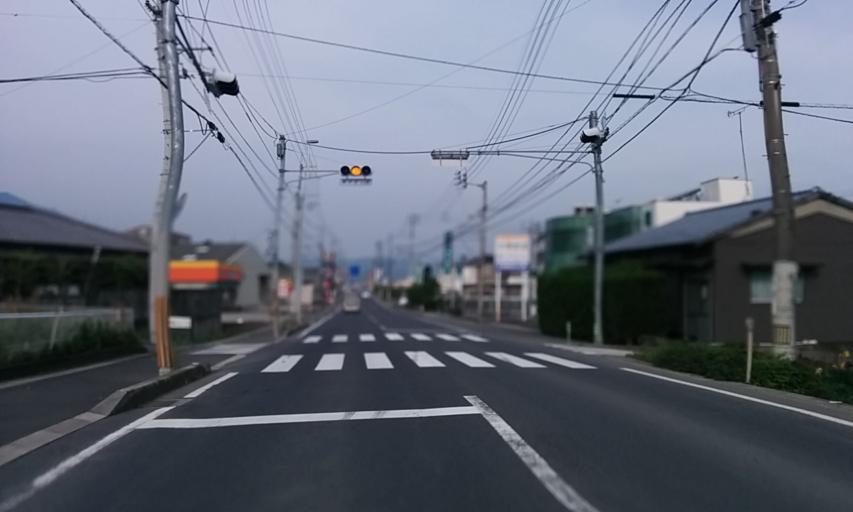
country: JP
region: Ehime
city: Niihama
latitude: 33.9577
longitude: 133.4366
